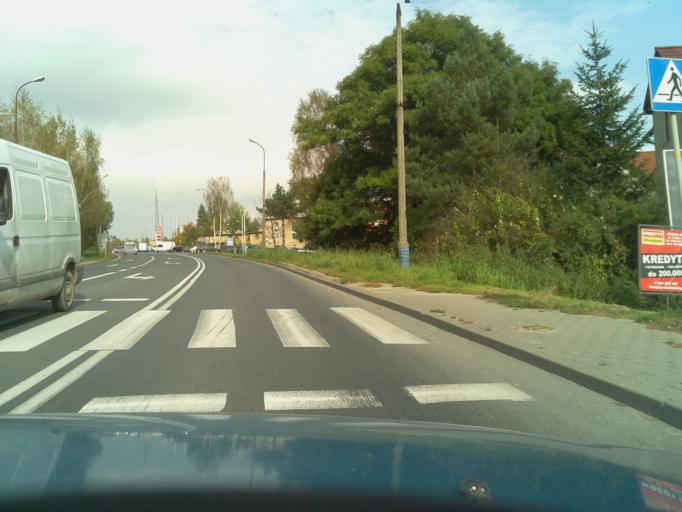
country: PL
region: Lower Silesian Voivodeship
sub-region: Jelenia Gora
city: Jelenia Gora
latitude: 50.8966
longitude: 15.7156
